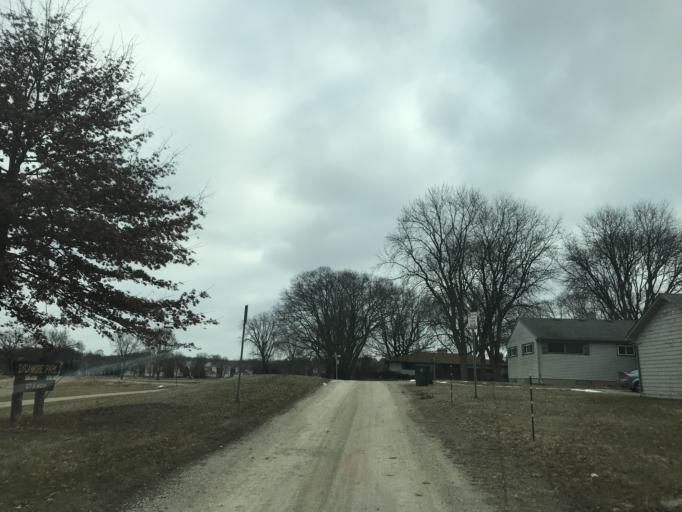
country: US
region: Wisconsin
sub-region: Dane County
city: Monona
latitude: 43.1102
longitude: -89.3031
